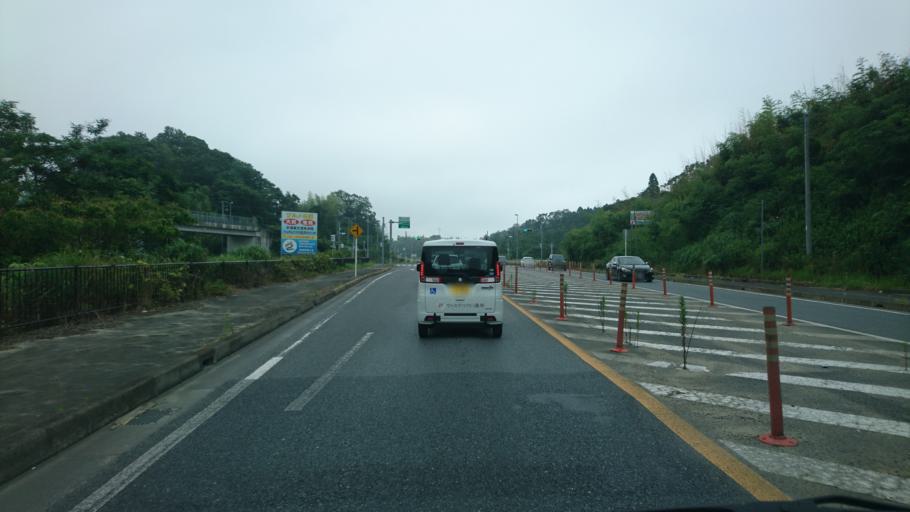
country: JP
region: Chiba
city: Kimitsu
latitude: 35.2516
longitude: 139.8853
